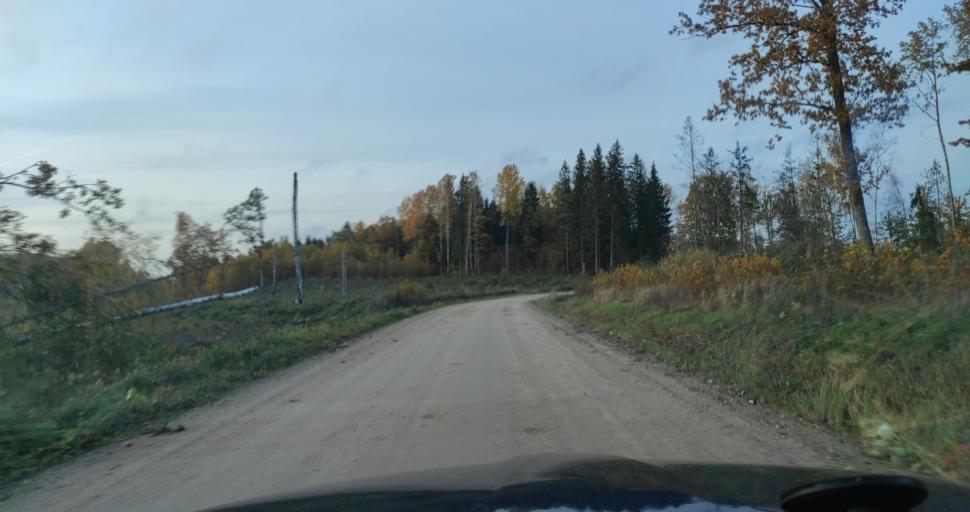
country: LV
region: Vainode
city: Vainode
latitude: 56.6329
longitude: 21.8140
